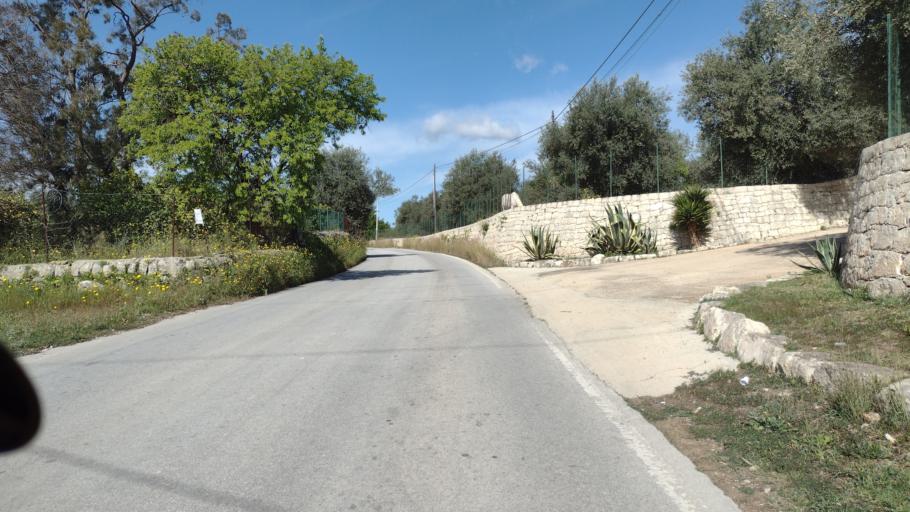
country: IT
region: Sicily
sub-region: Provincia di Siracusa
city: Noto
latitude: 36.8866
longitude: 15.0552
